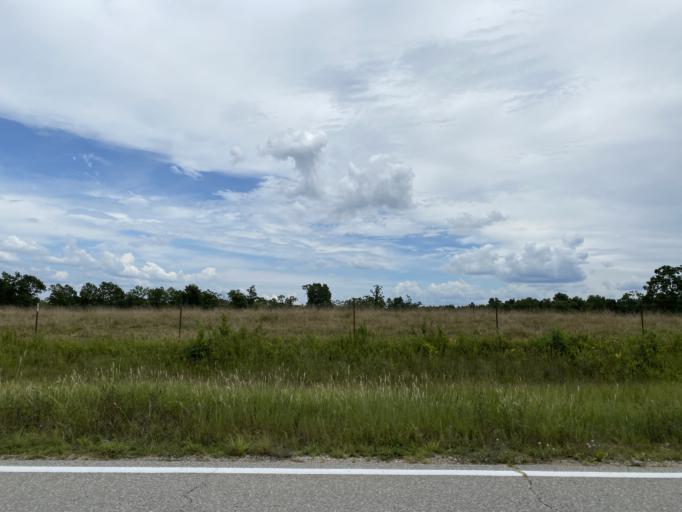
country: US
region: Arkansas
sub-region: Fulton County
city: Salem
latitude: 36.4236
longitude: -91.7103
